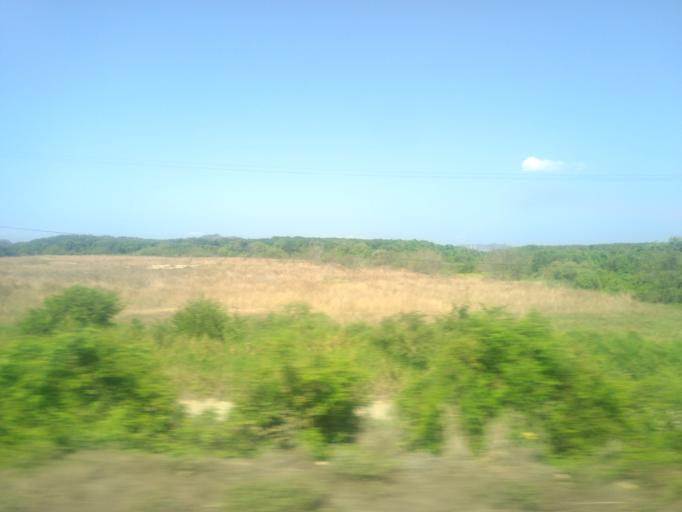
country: MX
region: Colima
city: El Colomo
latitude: 19.0407
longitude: -104.2588
